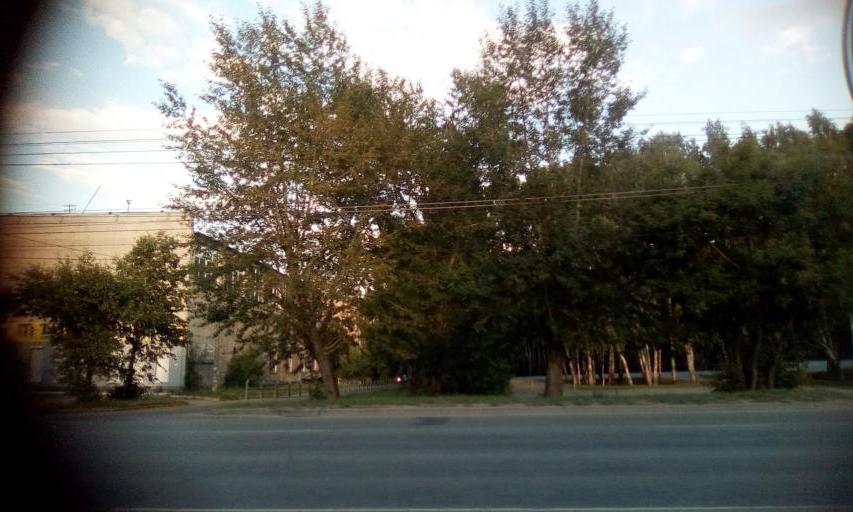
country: RU
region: Chelyabinsk
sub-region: Gorod Chelyabinsk
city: Chelyabinsk
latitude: 55.1193
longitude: 61.3623
